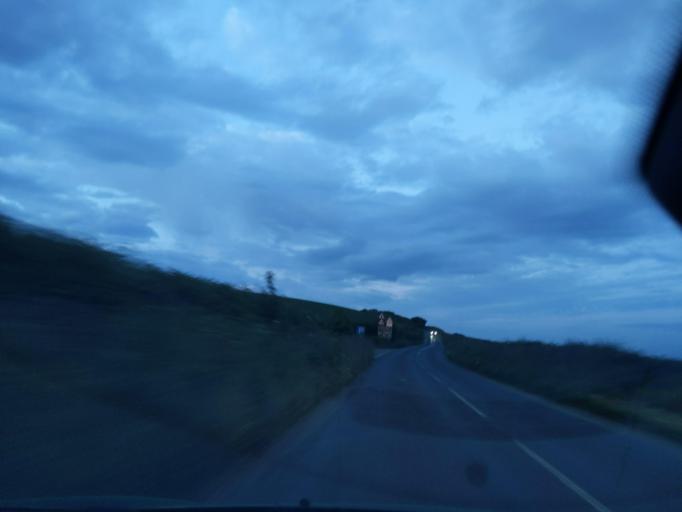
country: GB
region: England
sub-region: Cornwall
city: Wadebridge
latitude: 50.5761
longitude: -4.8109
